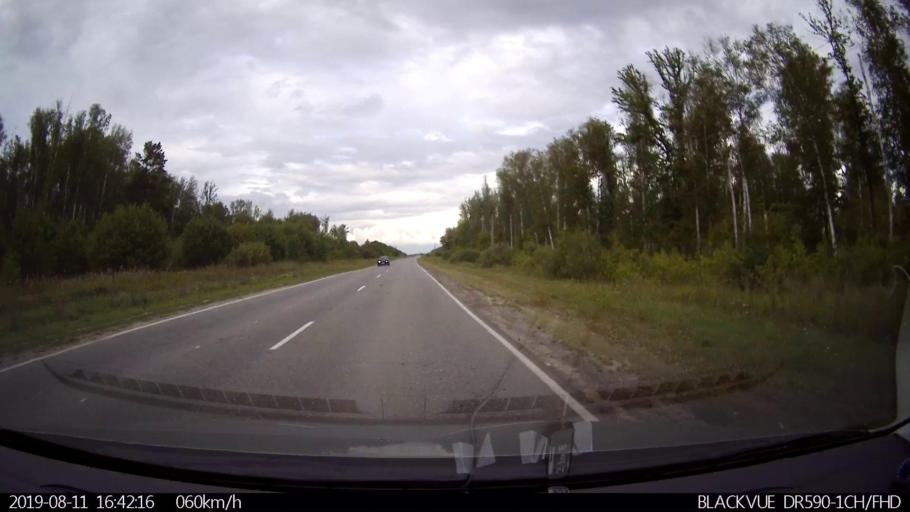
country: RU
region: Ulyanovsk
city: Mayna
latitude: 54.1592
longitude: 47.6609
